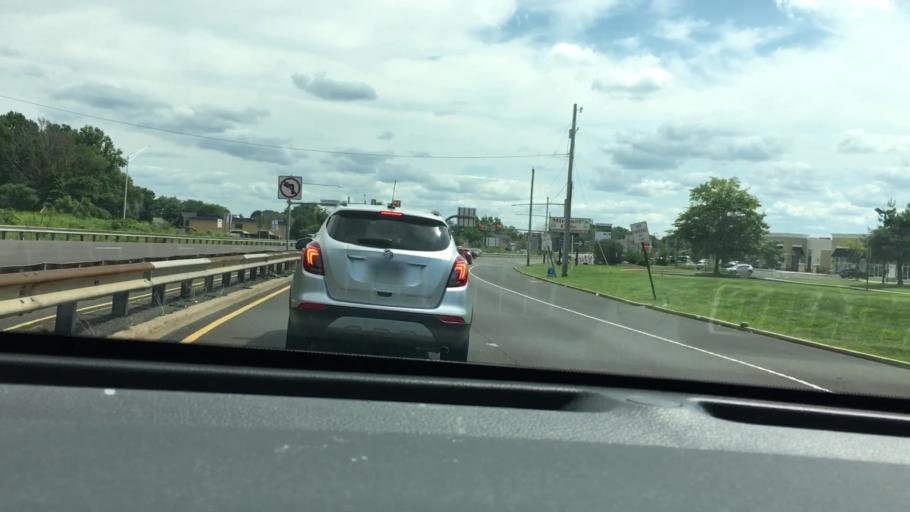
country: US
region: Pennsylvania
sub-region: Bucks County
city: Trevose
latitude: 40.1274
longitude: -74.9645
